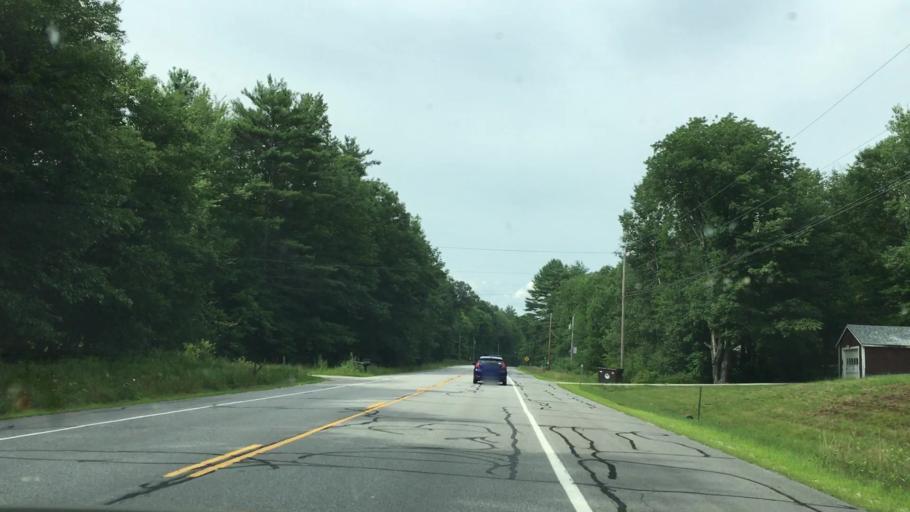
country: US
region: New Hampshire
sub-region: Hillsborough County
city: Hillsborough
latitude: 43.0889
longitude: -71.9193
